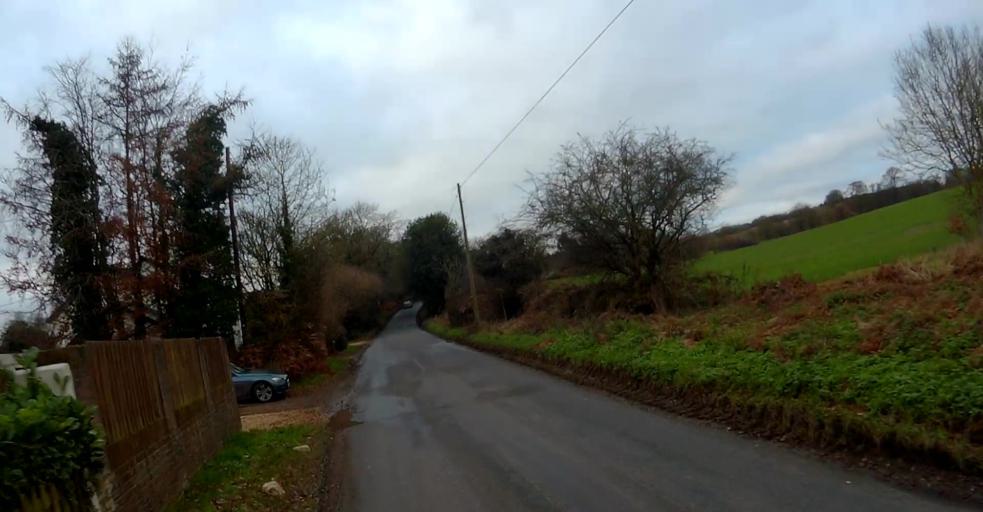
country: GB
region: England
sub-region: Hampshire
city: Basingstoke
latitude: 51.1911
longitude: -1.1580
